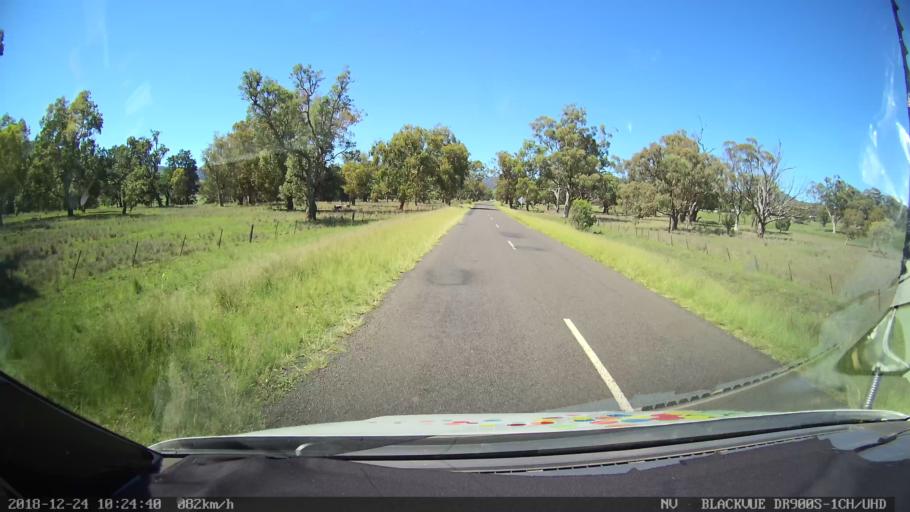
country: AU
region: New South Wales
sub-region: Liverpool Plains
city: Quirindi
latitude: -31.7894
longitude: 150.5317
